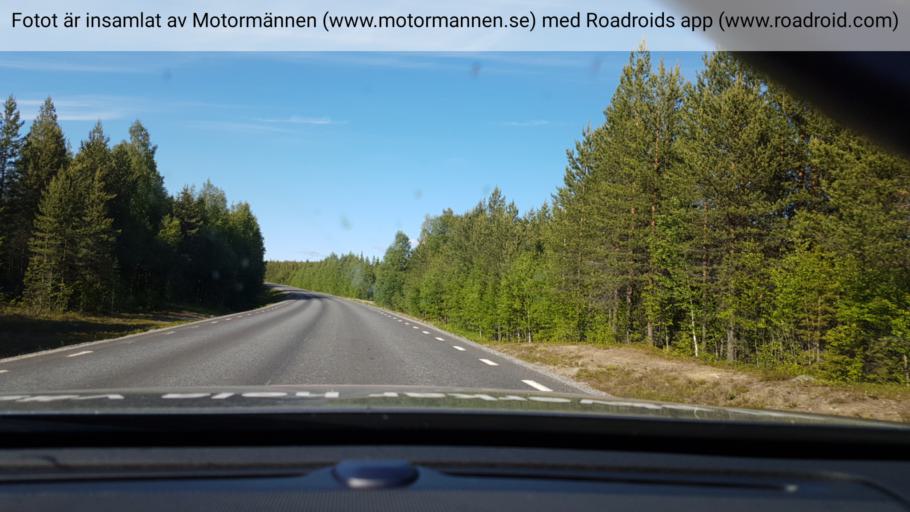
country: SE
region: Vaesterbotten
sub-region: Lycksele Kommun
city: Lycksele
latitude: 64.7796
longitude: 18.7345
